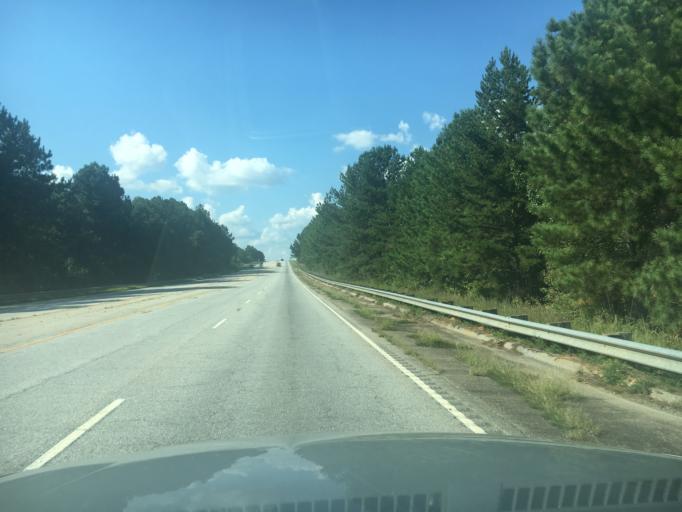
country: US
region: South Carolina
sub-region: Greenwood County
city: Ware Shoals
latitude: 34.4169
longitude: -82.2313
